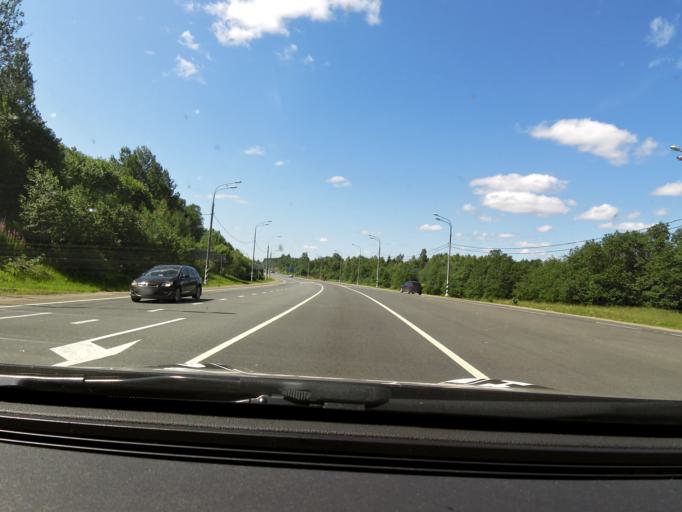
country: RU
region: Novgorod
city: Valday
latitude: 57.9910
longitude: 33.1970
